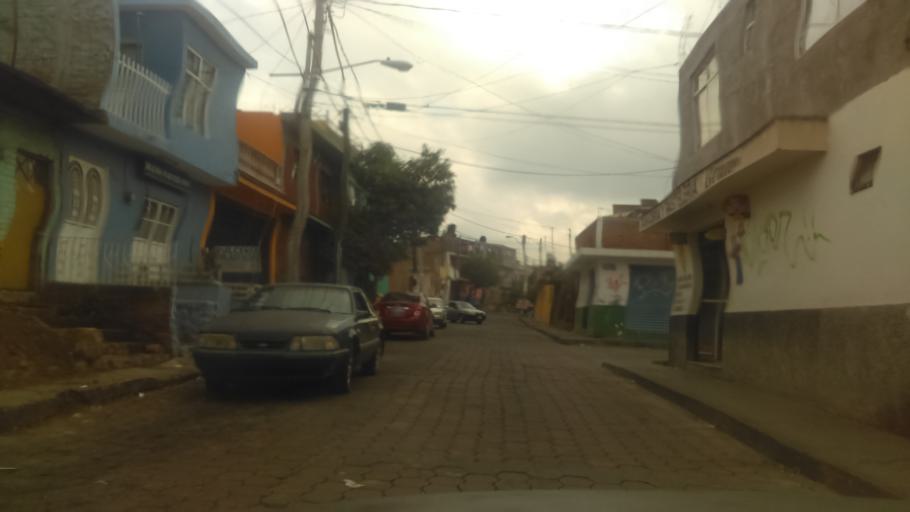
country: MX
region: Michoacan
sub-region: Morelia
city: Montana Monarca (Punta Altozano)
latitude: 19.6722
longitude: -101.1889
